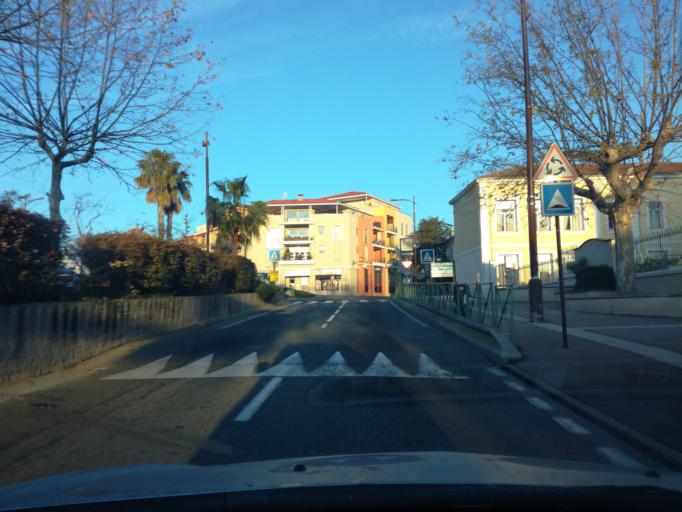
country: FR
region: Provence-Alpes-Cote d'Azur
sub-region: Departement du Var
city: Frejus
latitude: 43.4341
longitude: 6.7384
